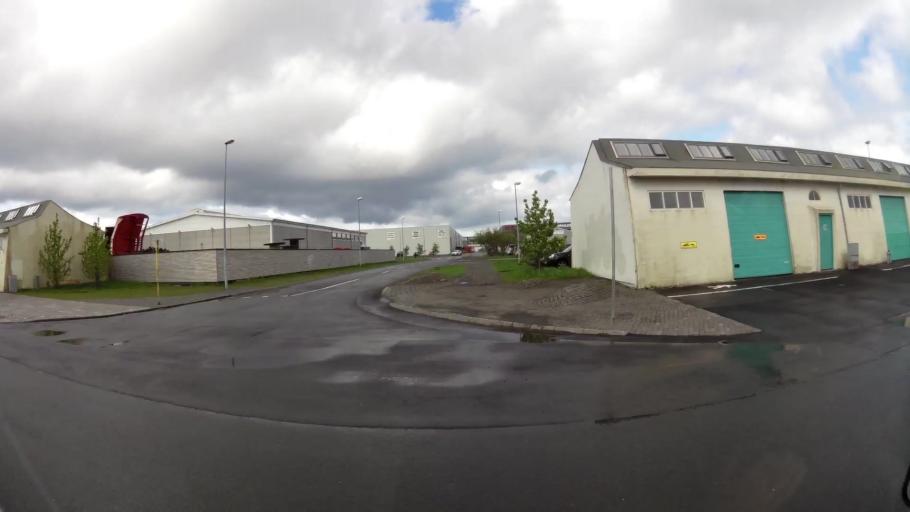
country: IS
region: Capital Region
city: Seltjarnarnes
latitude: 64.1539
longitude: -21.9469
